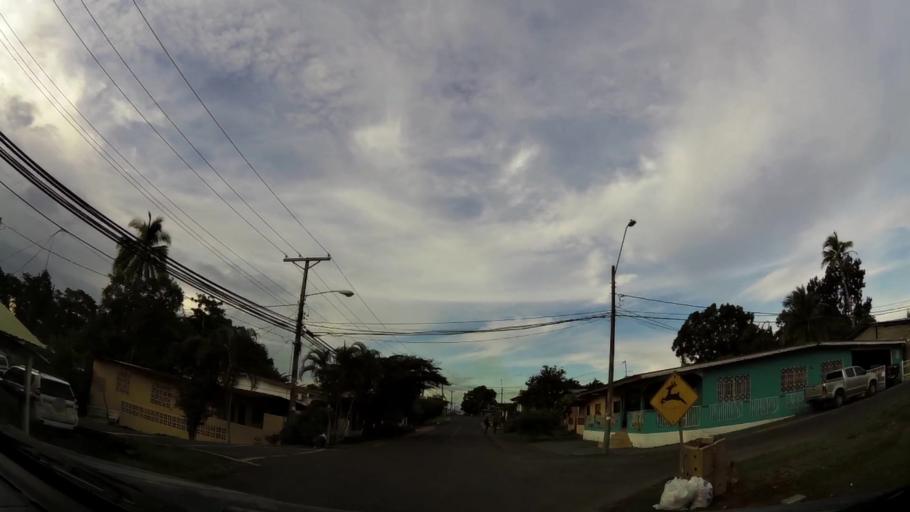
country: PA
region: Panama
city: La Chorrera
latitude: 8.8837
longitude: -79.7816
